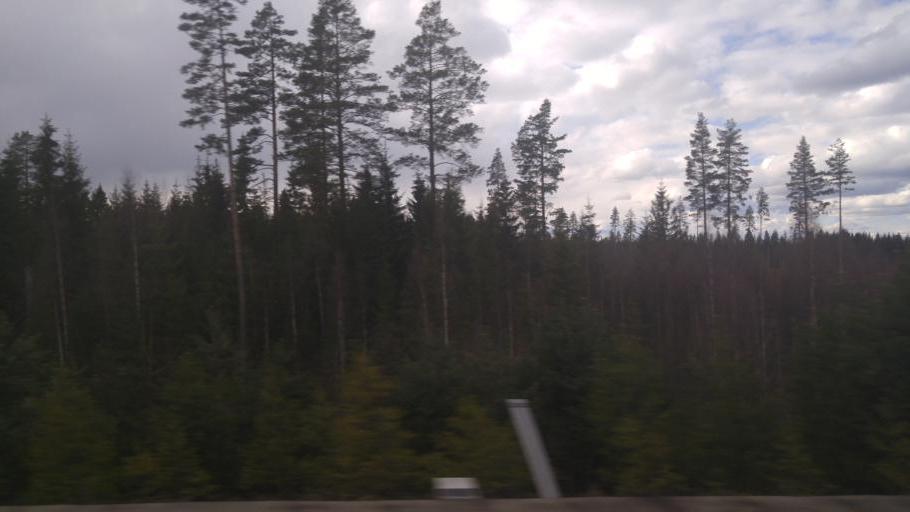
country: NO
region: Akershus
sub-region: Eidsvoll
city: Raholt
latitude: 60.2608
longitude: 11.1373
